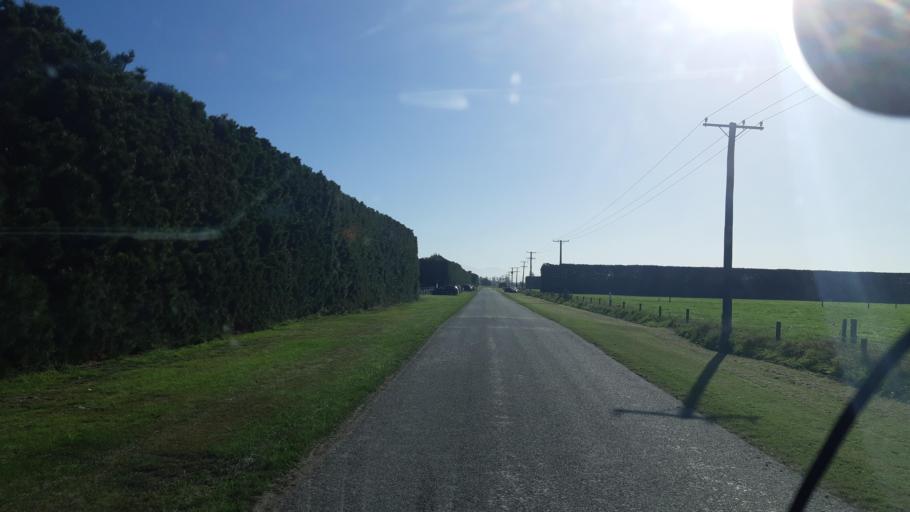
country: NZ
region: Canterbury
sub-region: Selwyn District
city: Darfield
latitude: -43.6096
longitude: 172.1373
